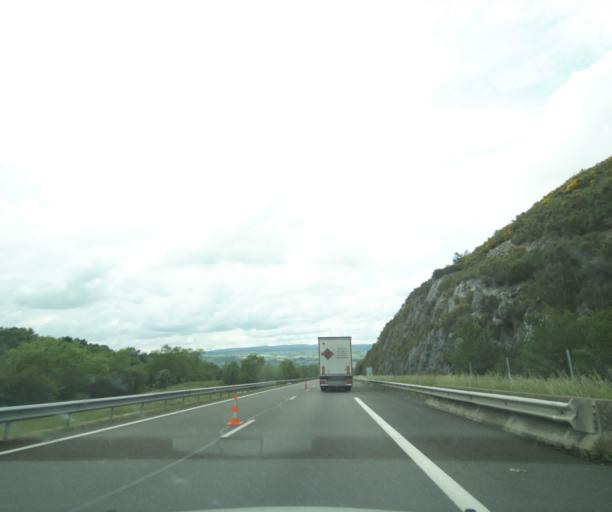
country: FR
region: Auvergne
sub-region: Departement de l'Allier
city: Ebreuil
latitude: 46.1116
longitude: 3.1340
